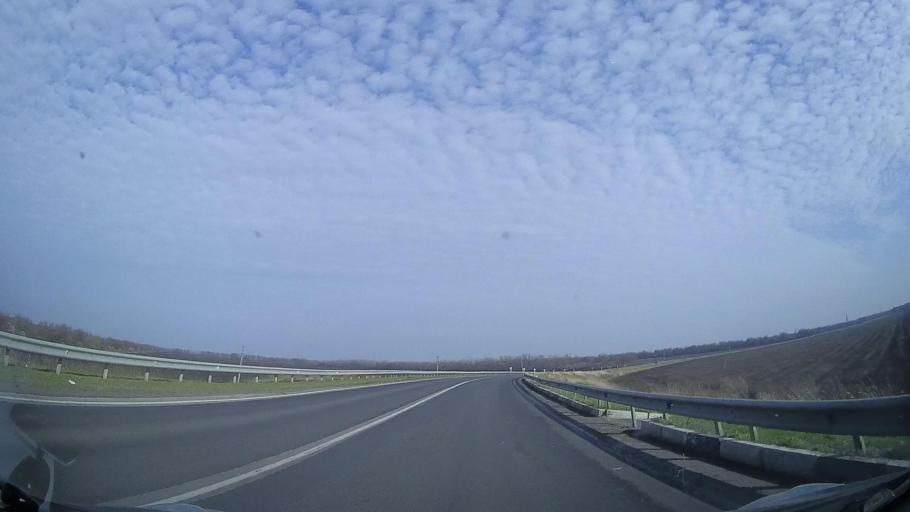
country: RU
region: Rostov
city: Tselina
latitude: 46.5298
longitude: 41.1690
